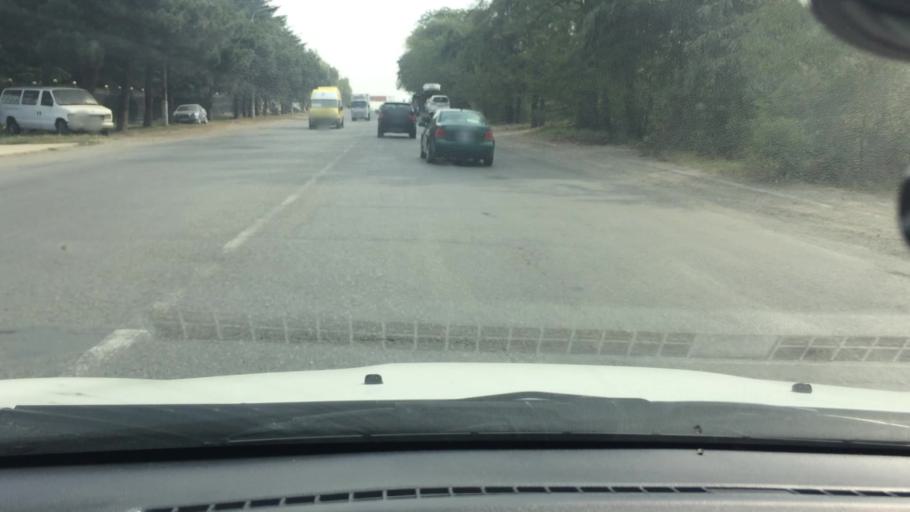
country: GE
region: T'bilisi
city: Tbilisi
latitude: 41.6429
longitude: 44.9128
